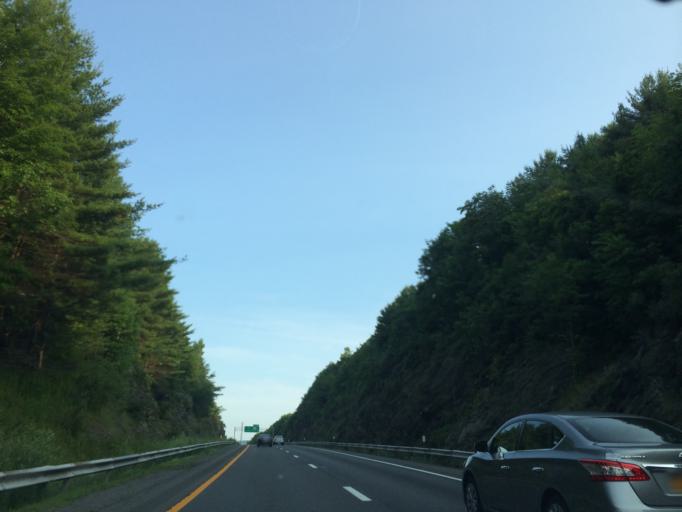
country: US
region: New York
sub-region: Columbia County
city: Chatham
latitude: 42.4271
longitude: -73.5534
